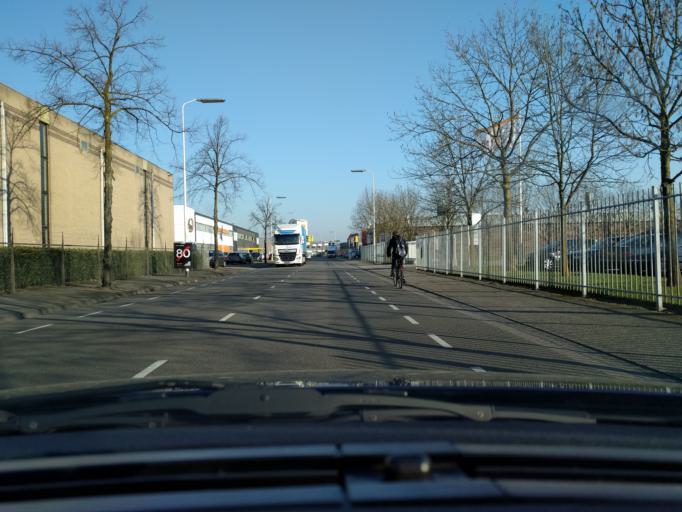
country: NL
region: North Brabant
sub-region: Gemeente Eindhoven
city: Eindhoven
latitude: 51.4300
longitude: 5.4465
